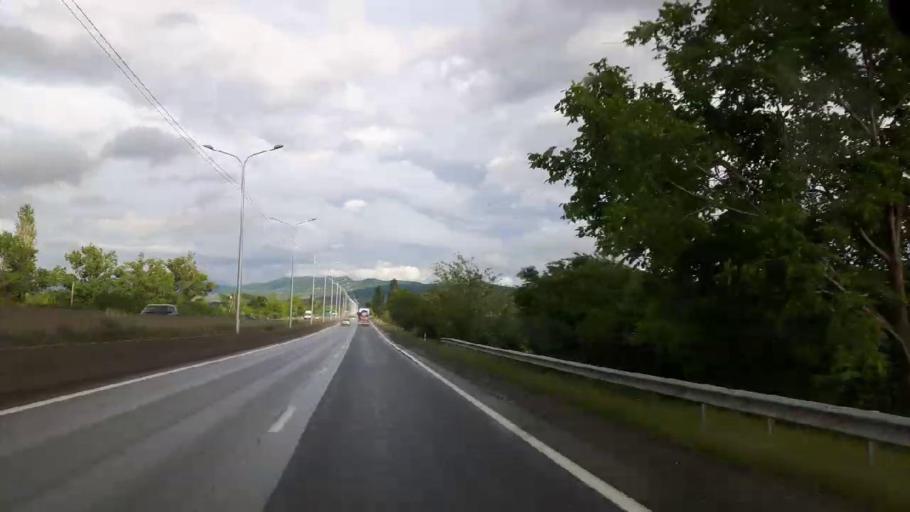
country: GE
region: Shida Kartli
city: Kaspi
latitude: 41.9249
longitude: 44.5390
